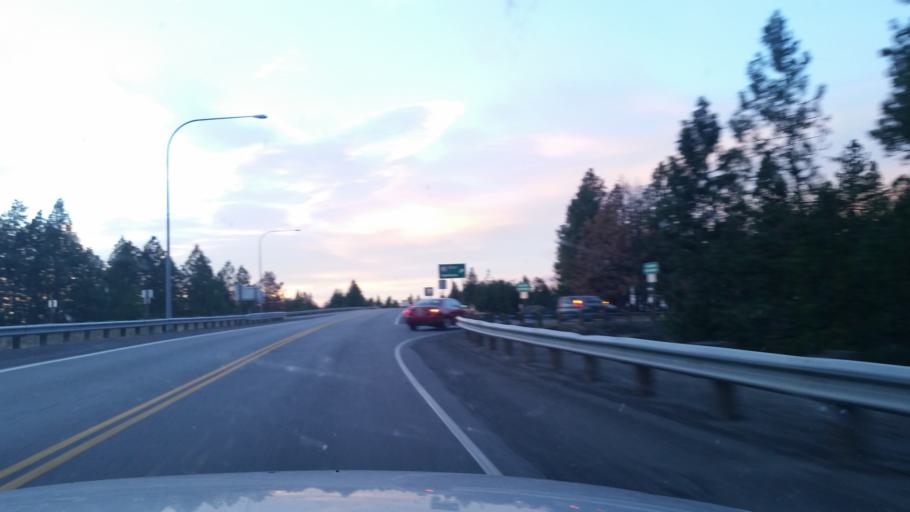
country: US
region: Washington
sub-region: Spokane County
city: Spokane
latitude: 47.6185
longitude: -117.5007
